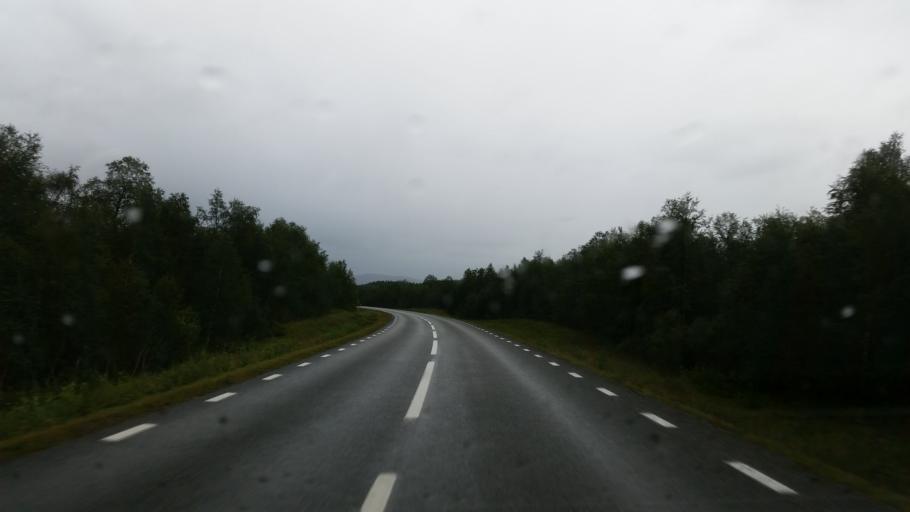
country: NO
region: Nordland
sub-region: Rana
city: Mo i Rana
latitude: 65.8852
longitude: 14.9878
